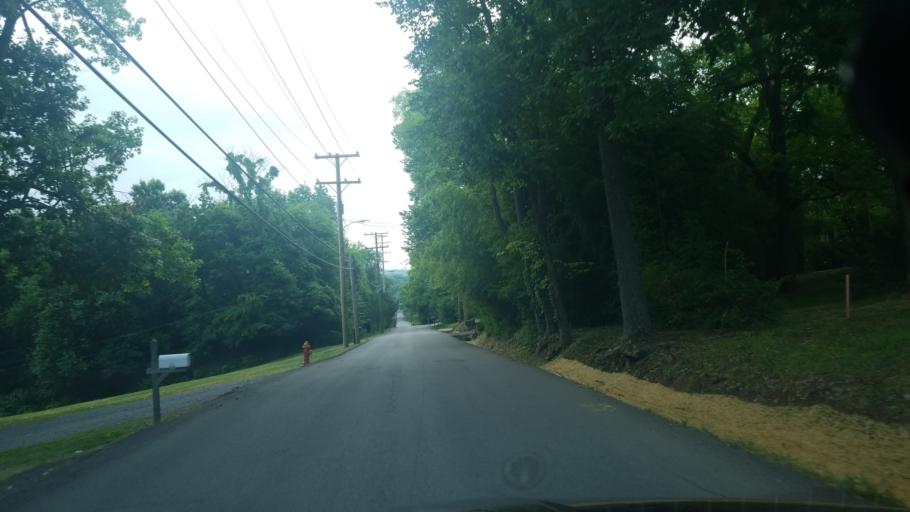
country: US
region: Tennessee
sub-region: Davidson County
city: Nashville
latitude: 36.2284
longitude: -86.7397
